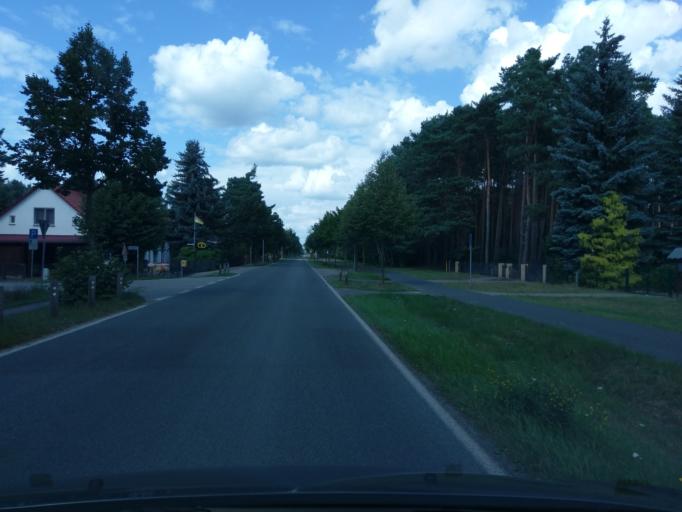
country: DE
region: Brandenburg
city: Borkheide
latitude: 52.2203
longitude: 12.8593
